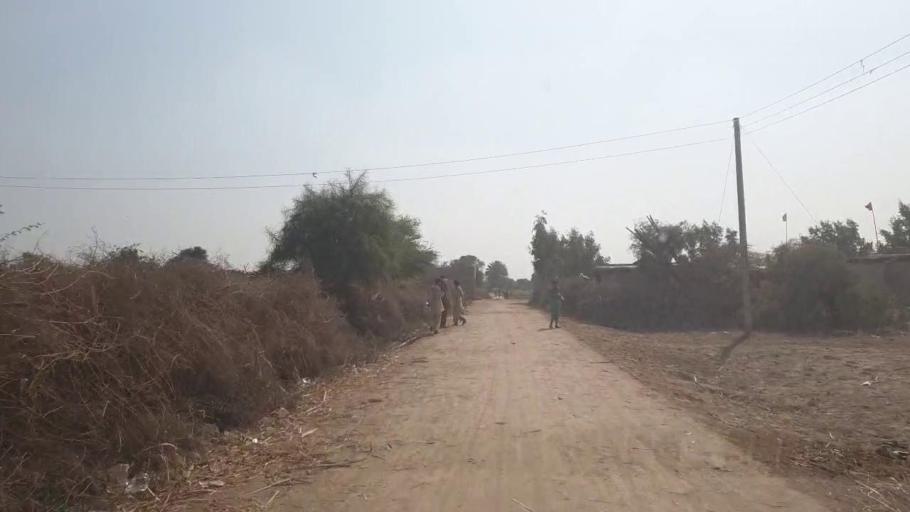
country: PK
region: Sindh
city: Mirpur Khas
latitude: 25.4820
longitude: 68.8940
